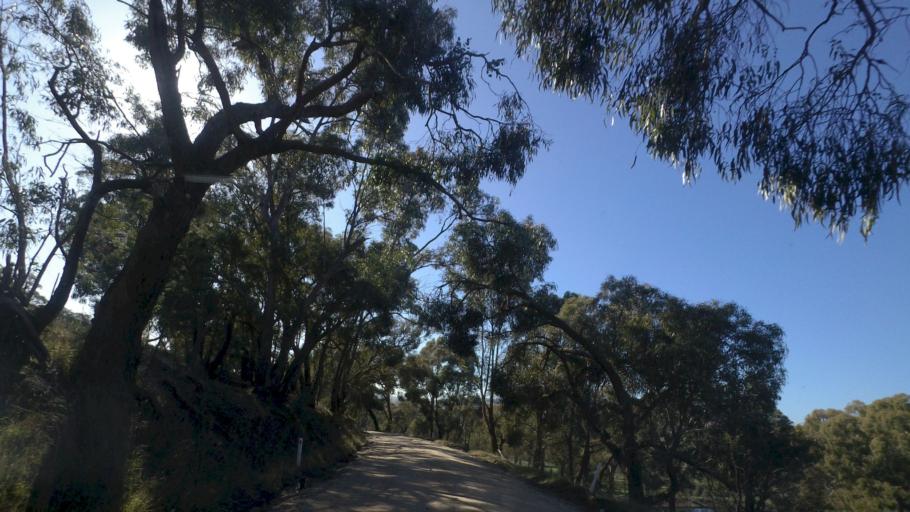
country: AU
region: Victoria
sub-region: Mount Alexander
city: Castlemaine
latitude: -37.1204
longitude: 144.4135
